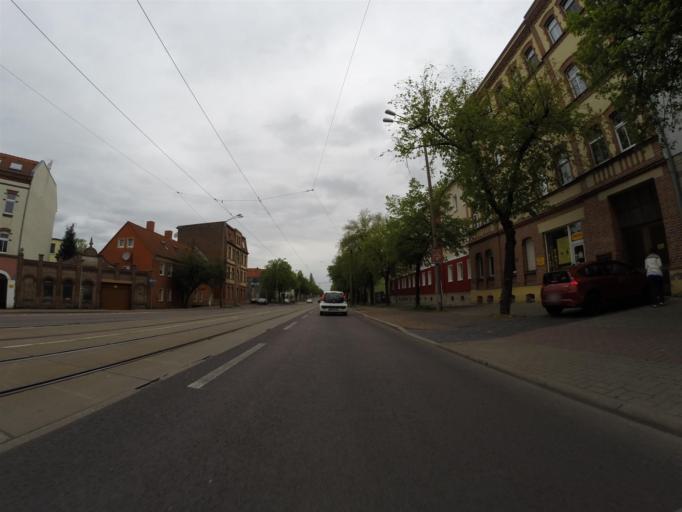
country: DE
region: Saxony-Anhalt
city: Schkopau
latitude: 51.4277
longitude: 11.9843
